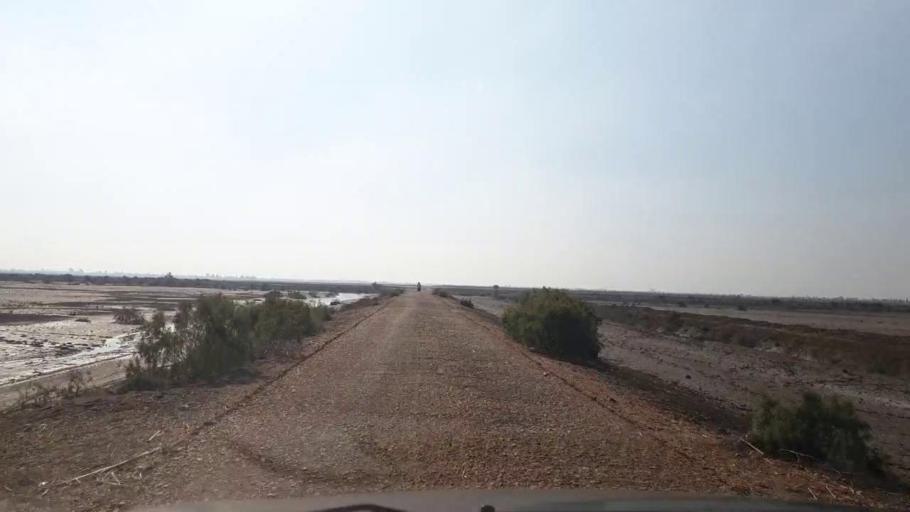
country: PK
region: Sindh
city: Sinjhoro
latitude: 26.0334
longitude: 68.7788
